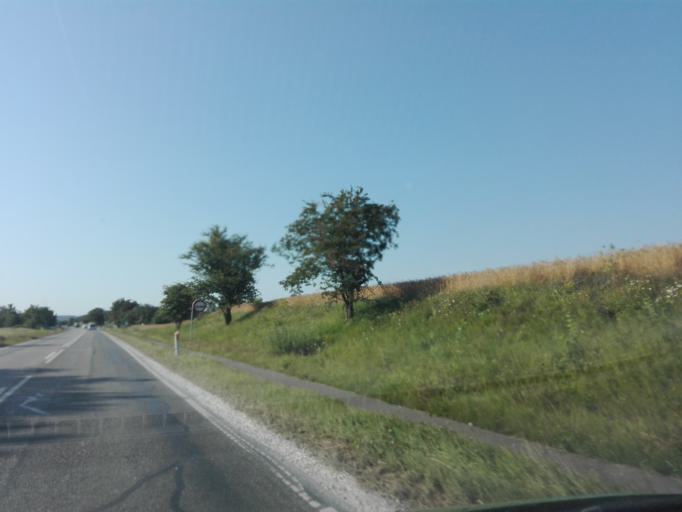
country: DK
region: Central Jutland
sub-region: Odder Kommune
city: Odder
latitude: 55.9559
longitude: 10.1921
